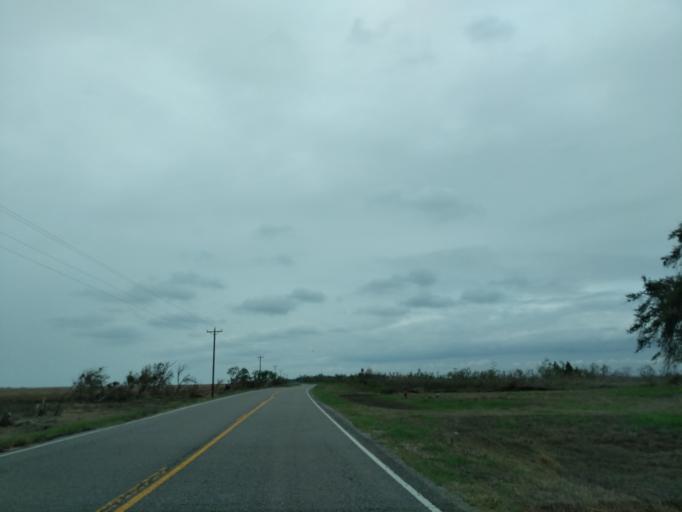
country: US
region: Louisiana
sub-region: Cameron Parish
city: Cameron
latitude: 29.7866
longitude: -93.1644
